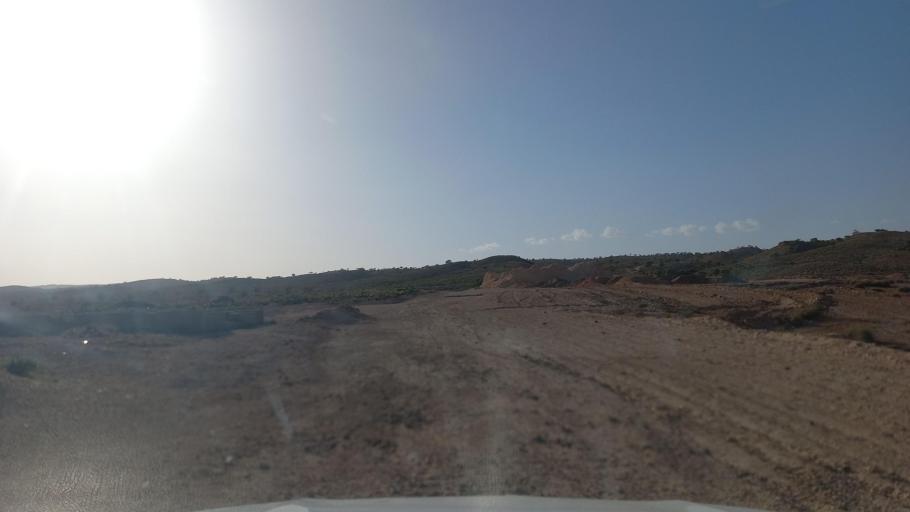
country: TN
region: Al Qasrayn
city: Sbiba
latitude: 35.3648
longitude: 8.9981
